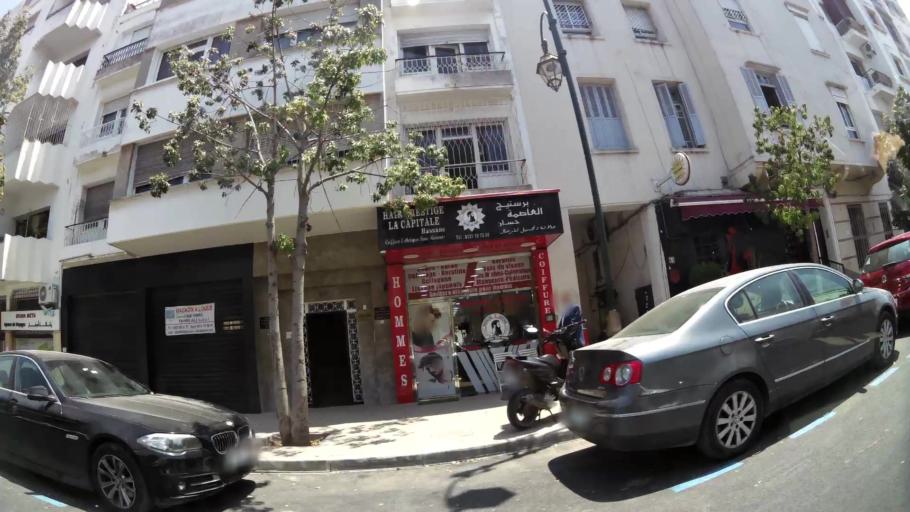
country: MA
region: Rabat-Sale-Zemmour-Zaer
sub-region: Rabat
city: Rabat
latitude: 34.0144
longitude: -6.8289
